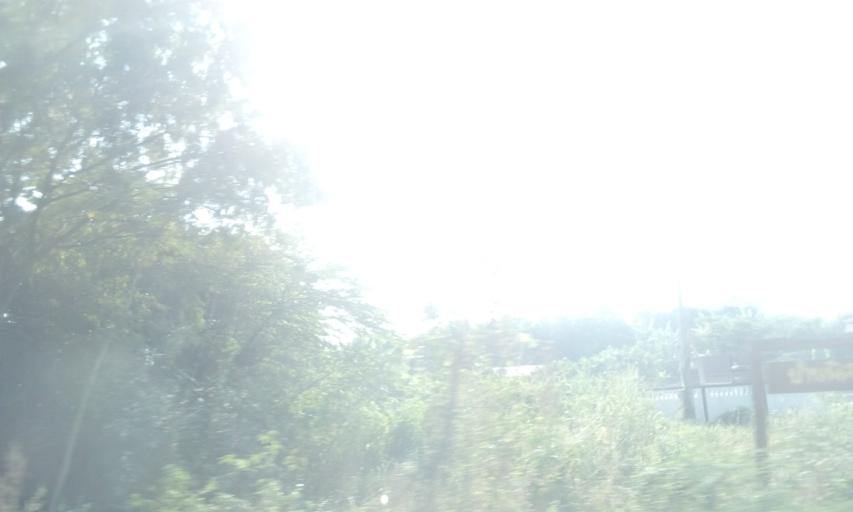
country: TH
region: Sing Buri
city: Phrom Buri
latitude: 14.7537
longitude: 100.4376
